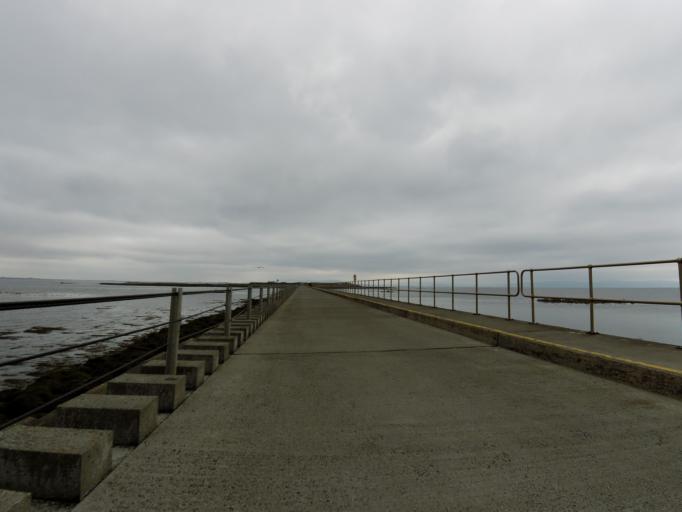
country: IE
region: Connaught
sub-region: County Galway
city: Gaillimh
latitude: 53.2603
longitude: -9.0558
